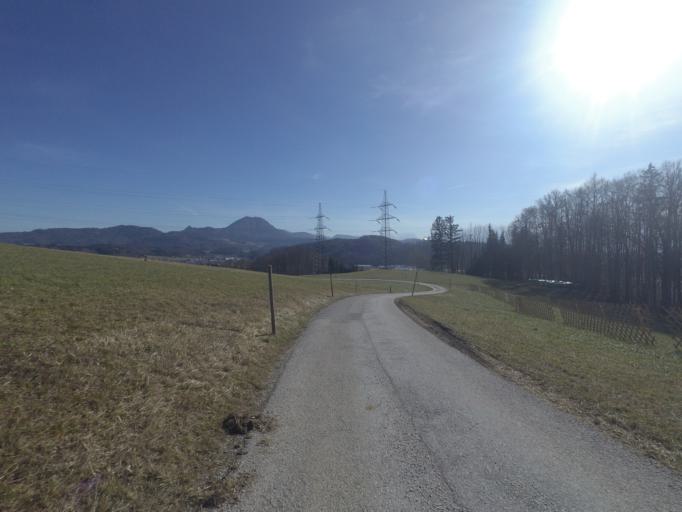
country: AT
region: Salzburg
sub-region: Politischer Bezirk Salzburg-Umgebung
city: Bergheim
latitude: 47.8508
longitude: 13.0347
